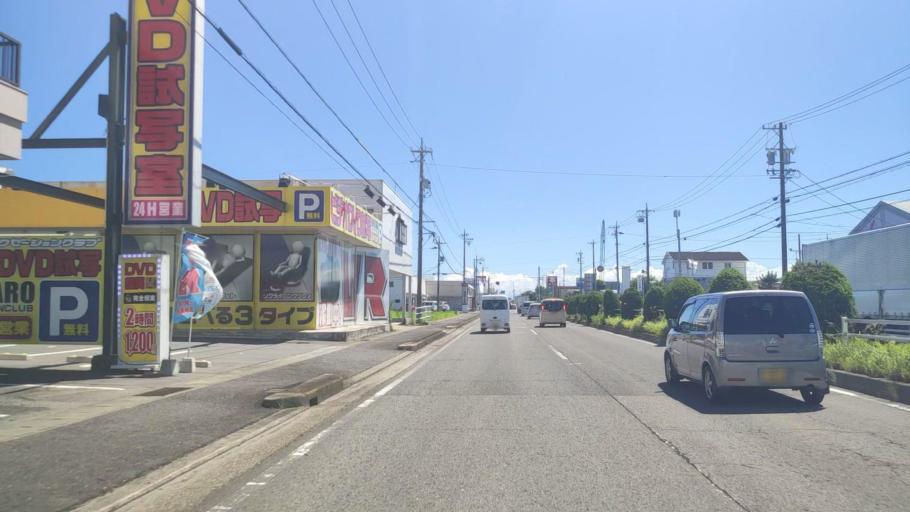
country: JP
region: Mie
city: Kawage
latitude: 34.8240
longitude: 136.5764
